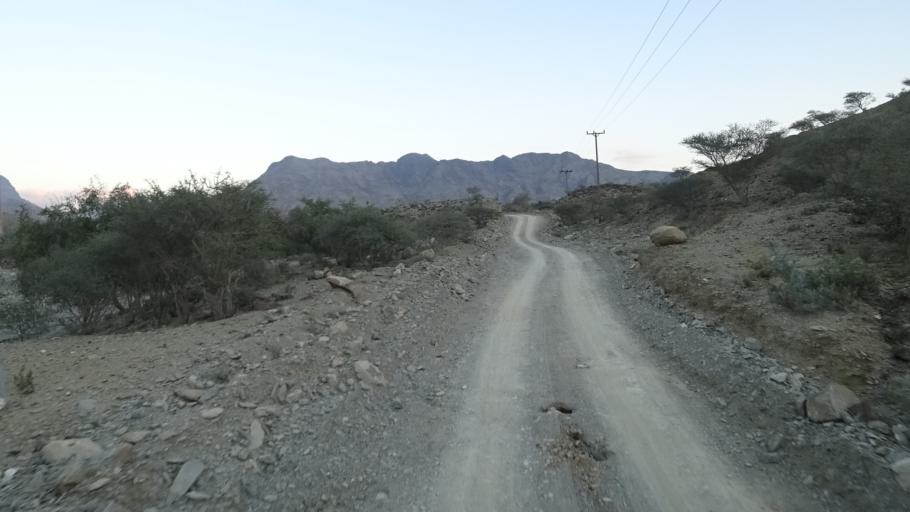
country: OM
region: Al Batinah
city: Rustaq
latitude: 23.2789
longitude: 57.3540
